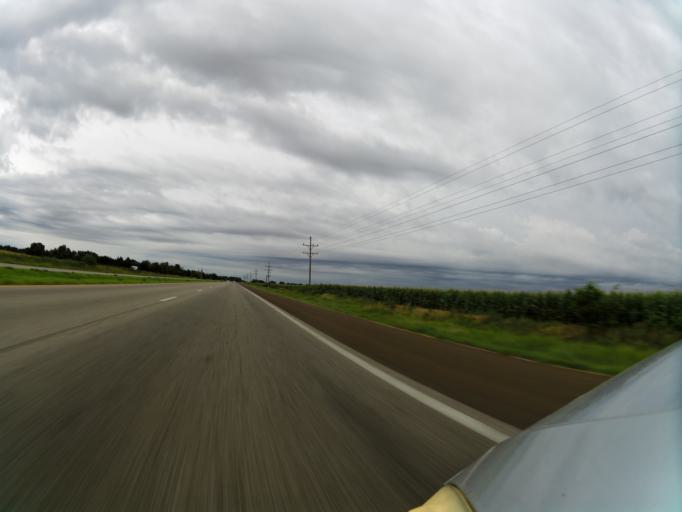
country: US
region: Kansas
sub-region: Reno County
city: South Hutchinson
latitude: 37.9974
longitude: -97.9404
